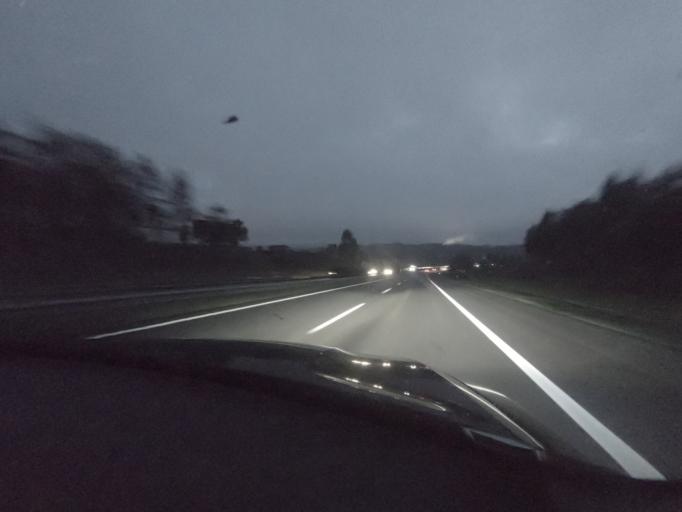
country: PT
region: Leiria
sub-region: Leiria
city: Caranguejeira
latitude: 39.8106
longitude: -8.7226
